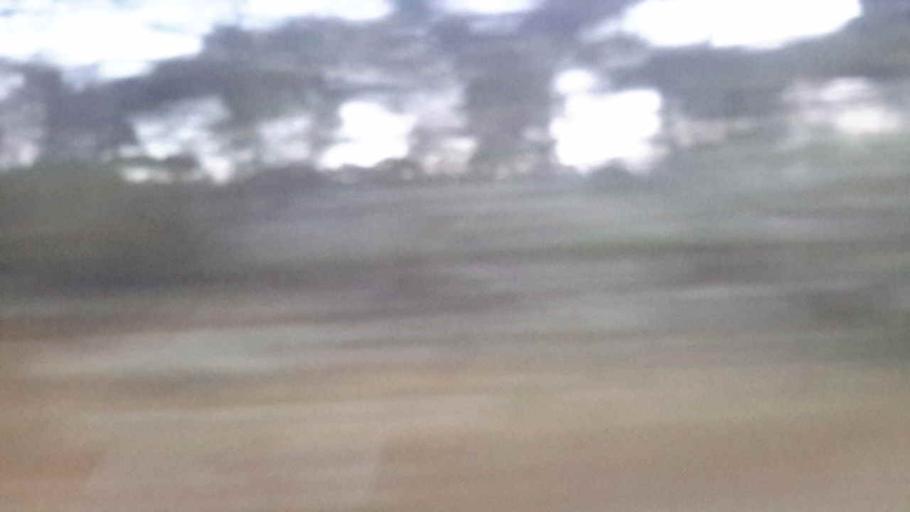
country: AU
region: New South Wales
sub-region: Wollongong
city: Mount Keira
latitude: -34.3820
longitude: 150.8345
